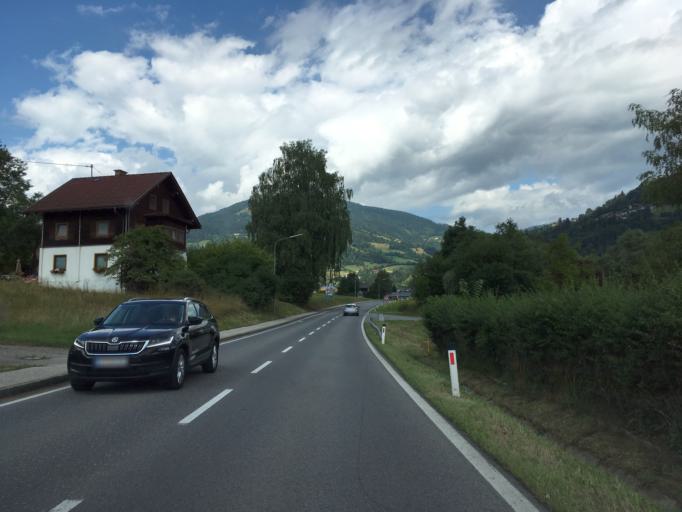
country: AT
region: Carinthia
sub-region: Politischer Bezirk Spittal an der Drau
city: Radenthein
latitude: 46.7929
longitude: 13.7233
